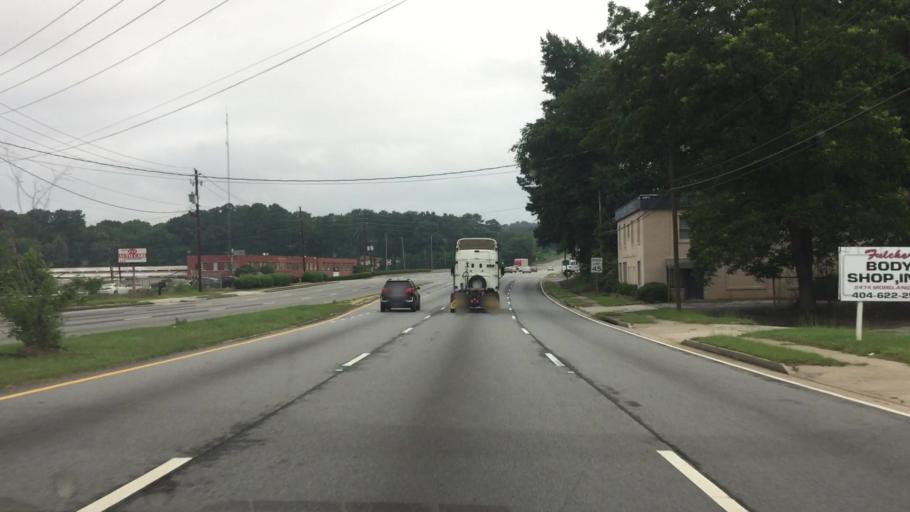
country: US
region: Georgia
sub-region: DeKalb County
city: Gresham Park
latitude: 33.6864
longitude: -84.3487
